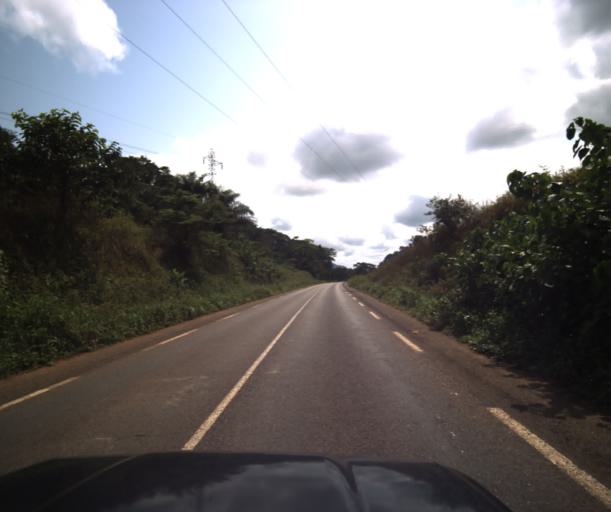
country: CM
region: Centre
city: Eseka
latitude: 3.8821
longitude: 10.6971
